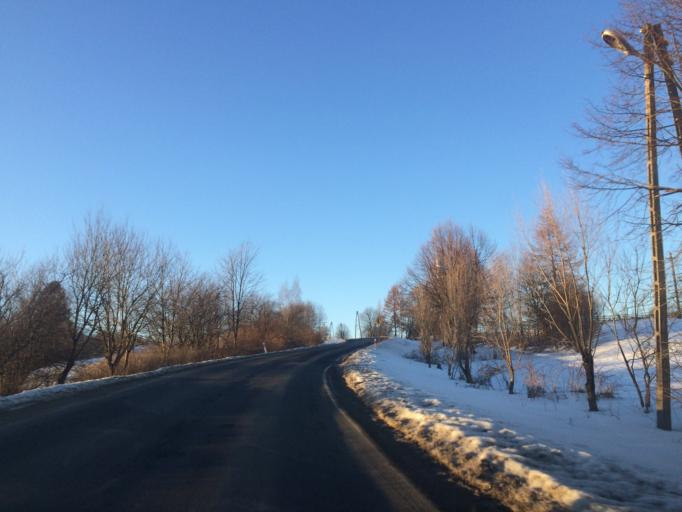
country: PL
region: Subcarpathian Voivodeship
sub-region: Powiat bieszczadzki
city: Lutowiska
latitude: 49.2585
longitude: 22.6847
